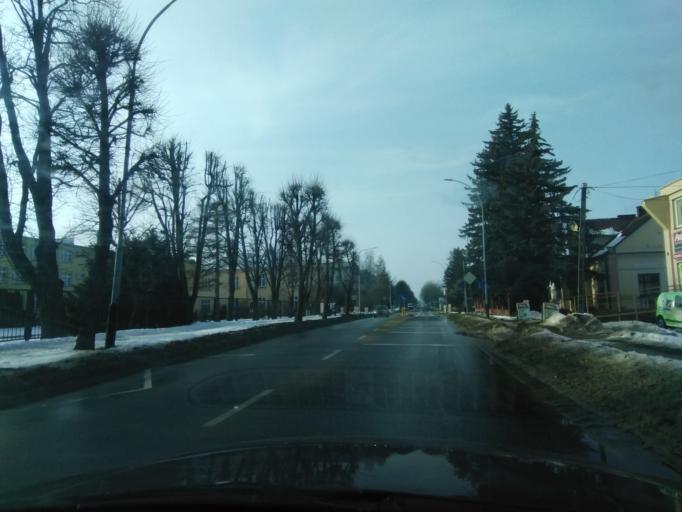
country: PL
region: Subcarpathian Voivodeship
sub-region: Krosno
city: Krosno
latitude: 49.6985
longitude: 21.7518
